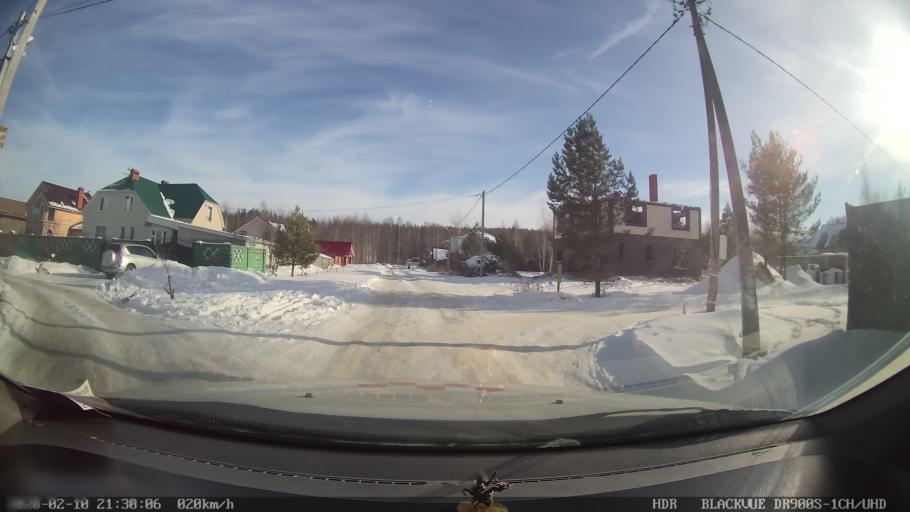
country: RU
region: Tatarstan
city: Vysokaya Gora
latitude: 55.7796
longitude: 49.2753
